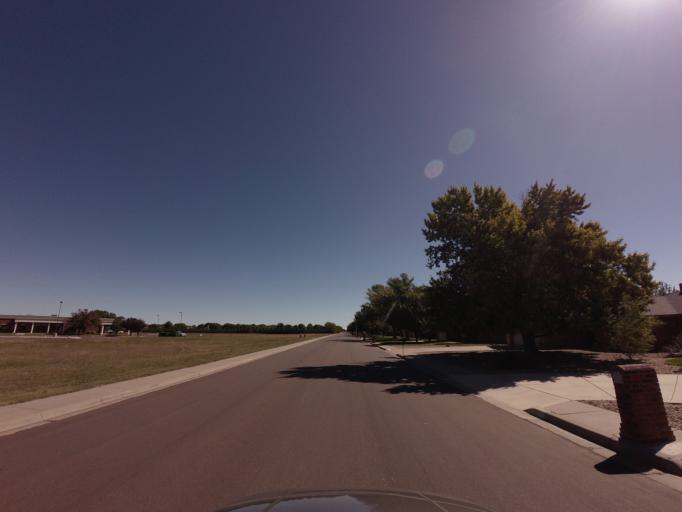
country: US
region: New Mexico
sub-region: Curry County
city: Clovis
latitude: 34.4232
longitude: -103.1778
